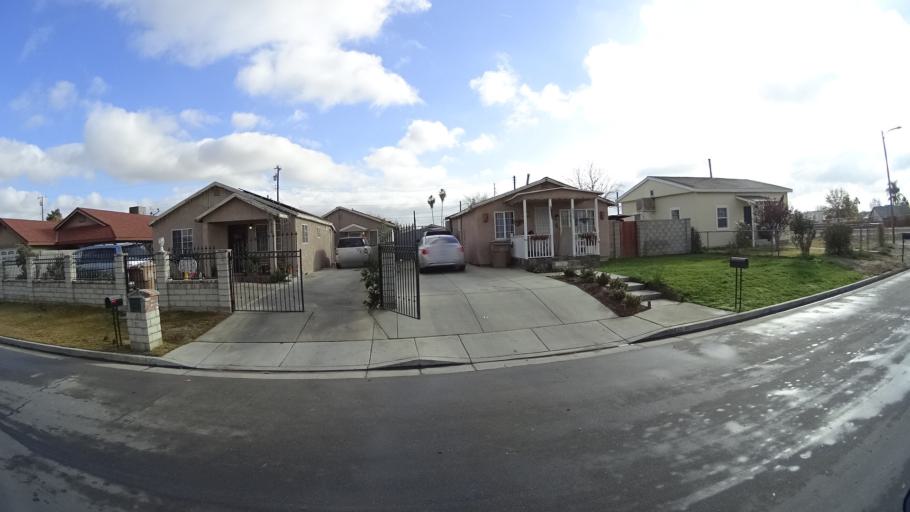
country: US
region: California
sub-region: Kern County
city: Greenfield
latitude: 35.2927
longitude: -119.0097
